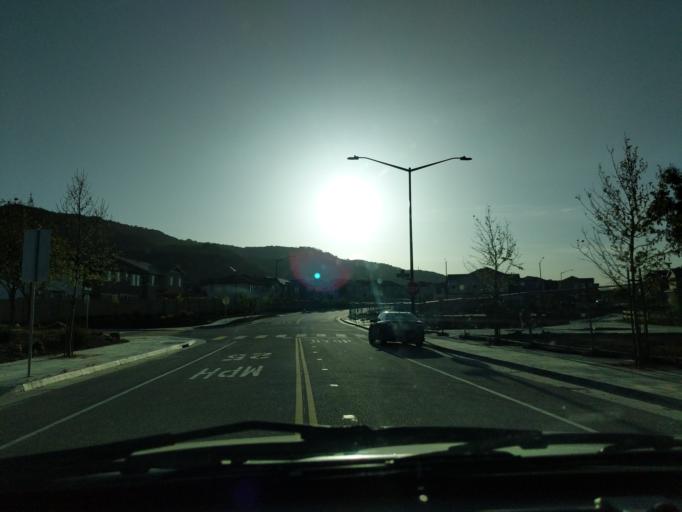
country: US
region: California
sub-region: Santa Clara County
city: Gilroy
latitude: 36.9907
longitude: -121.5809
